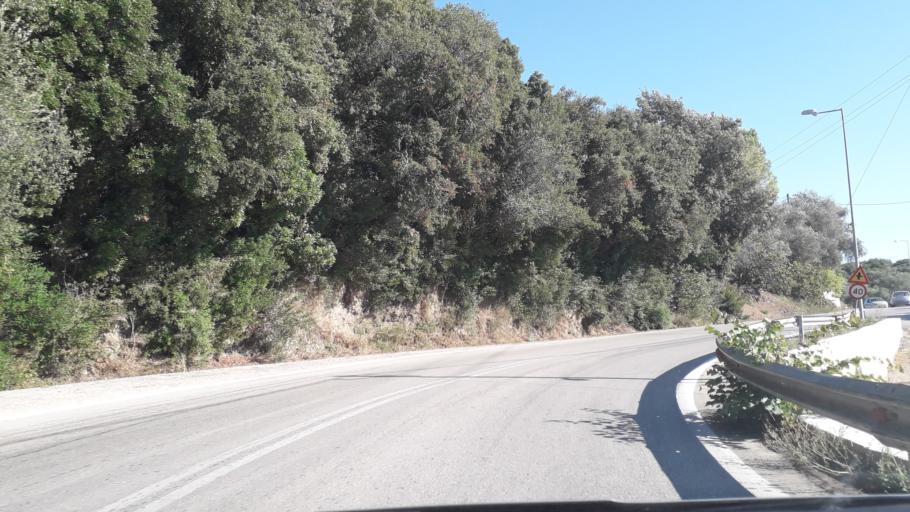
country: GR
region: Ionian Islands
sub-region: Nomos Kerkyras
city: Agios Matthaios
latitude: 39.4603
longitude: 19.9146
